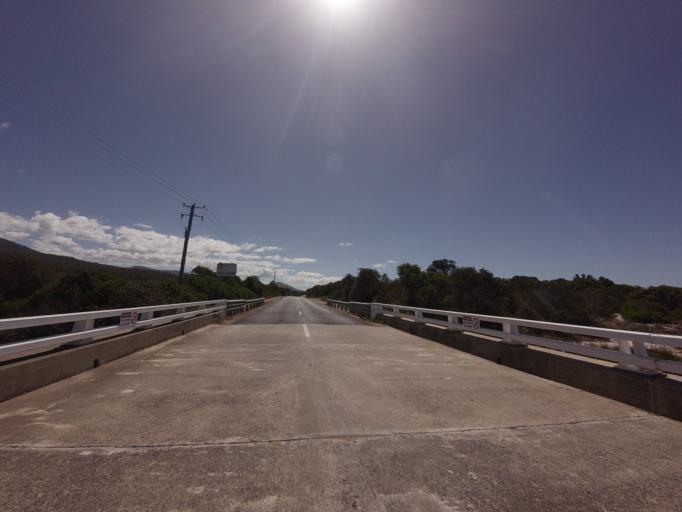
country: AU
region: Tasmania
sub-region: Break O'Day
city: St Helens
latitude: -41.8139
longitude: 148.2628
